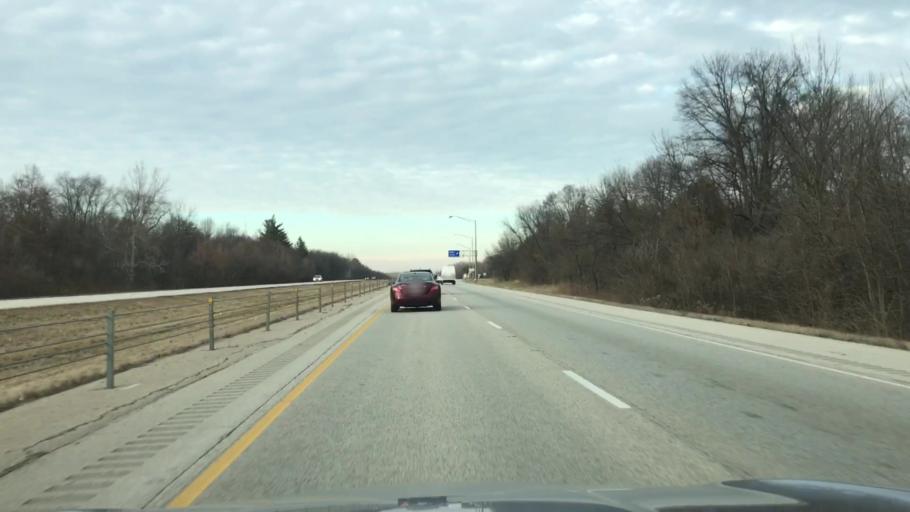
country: US
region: Illinois
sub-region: Sangamon County
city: Sherman
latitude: 39.8595
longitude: -89.5952
